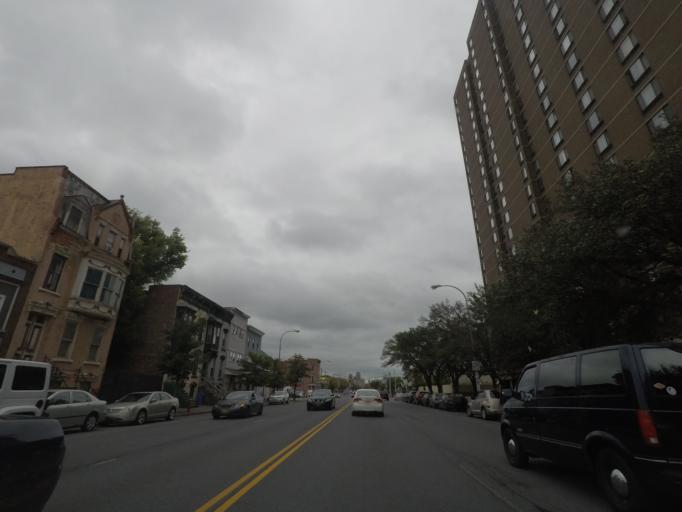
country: US
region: New York
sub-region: Albany County
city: West Albany
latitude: 42.6681
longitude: -73.7763
